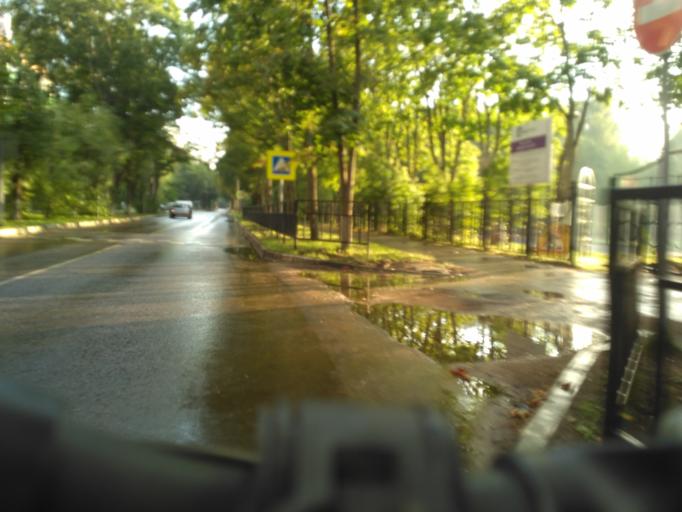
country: RU
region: Moskovskaya
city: Dubna
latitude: 56.7538
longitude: 37.1971
